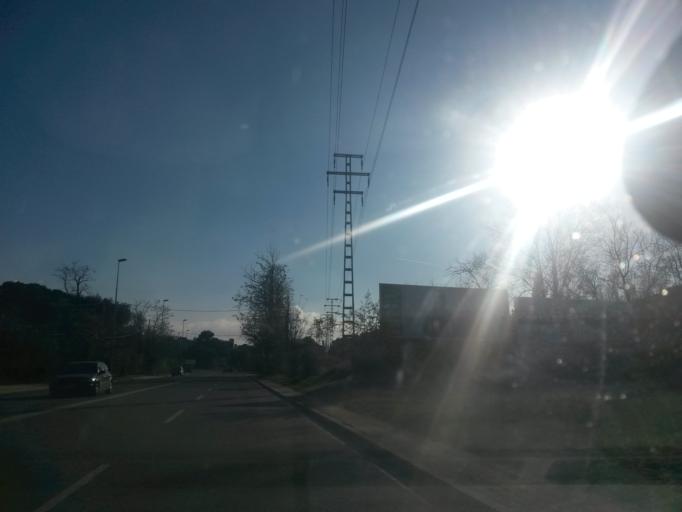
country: ES
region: Catalonia
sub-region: Provincia de Girona
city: Girona
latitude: 42.0027
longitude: 2.8159
